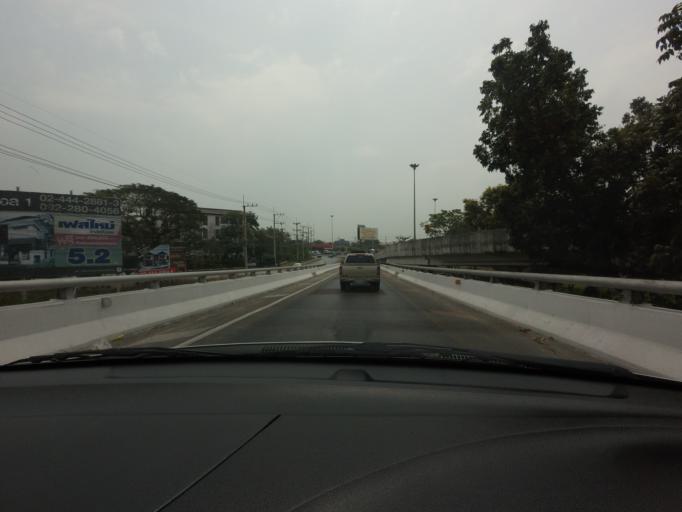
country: TH
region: Bangkok
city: Thawi Watthana
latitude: 13.7887
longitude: 100.3294
